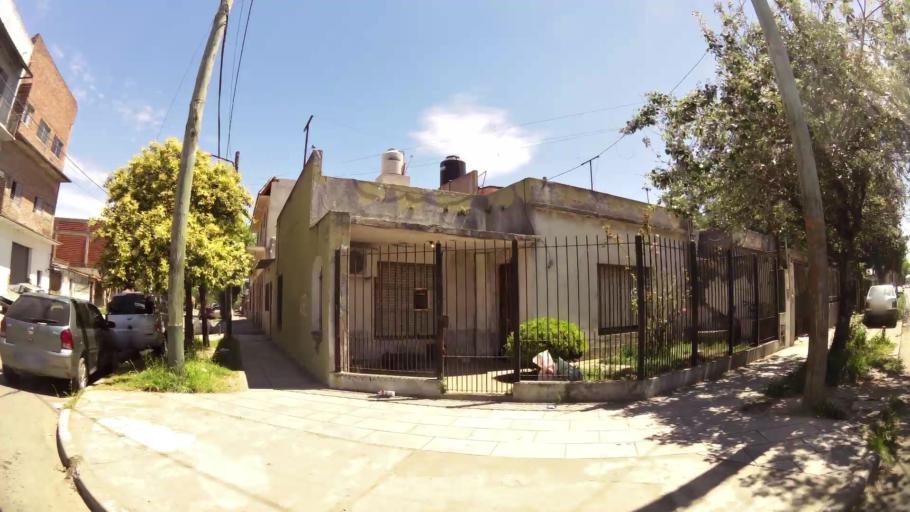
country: AR
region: Buenos Aires
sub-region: Partido de Quilmes
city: Quilmes
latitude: -34.7275
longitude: -58.3084
